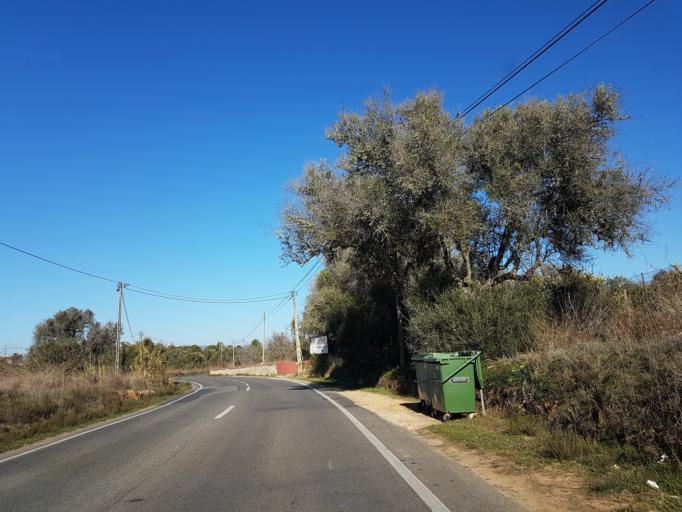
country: PT
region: Faro
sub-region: Lagoa
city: Carvoeiro
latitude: 37.1057
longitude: -8.4457
